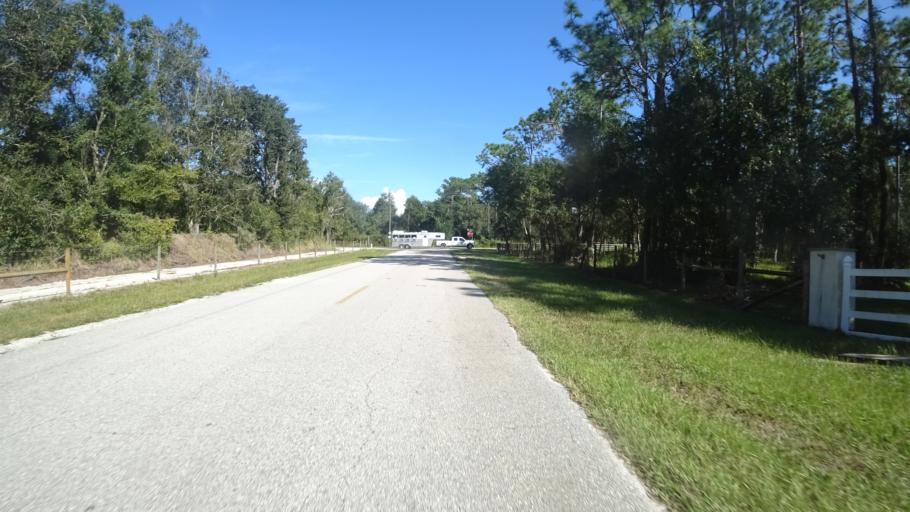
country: US
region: Florida
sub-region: Sarasota County
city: The Meadows
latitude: 27.4304
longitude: -82.2714
